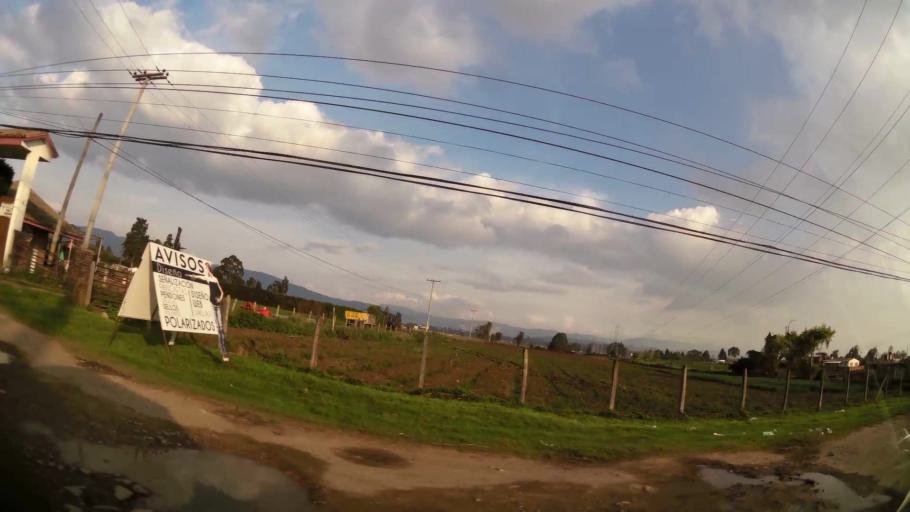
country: CO
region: Cundinamarca
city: Cota
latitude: 4.8183
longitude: -74.0948
